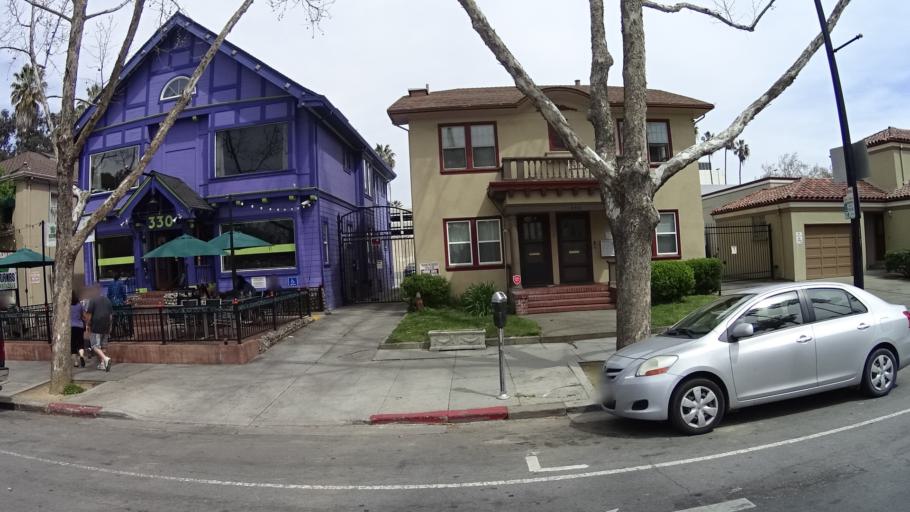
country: US
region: California
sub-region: Santa Clara County
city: San Jose
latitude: 37.3318
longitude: -121.8845
